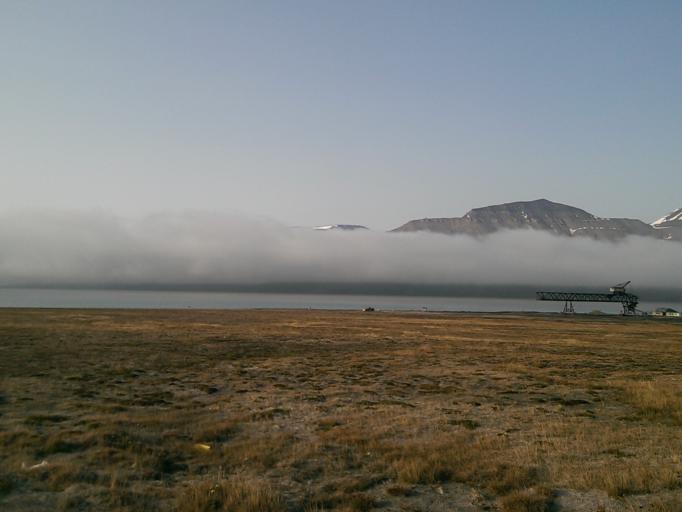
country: SJ
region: Svalbard
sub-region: Spitsbergen
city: Longyearbyen
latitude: 78.2444
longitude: 15.5201
